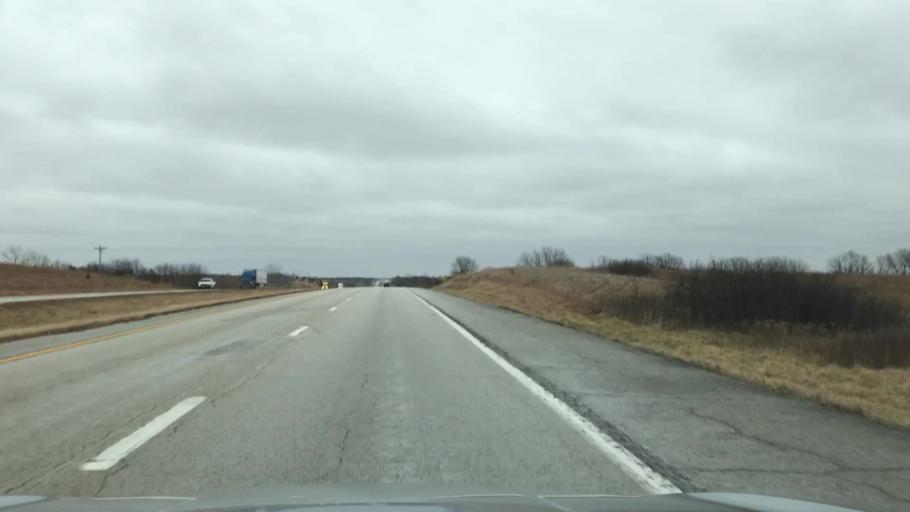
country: US
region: Missouri
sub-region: Clinton County
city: Cameron
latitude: 39.7509
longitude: -94.1408
